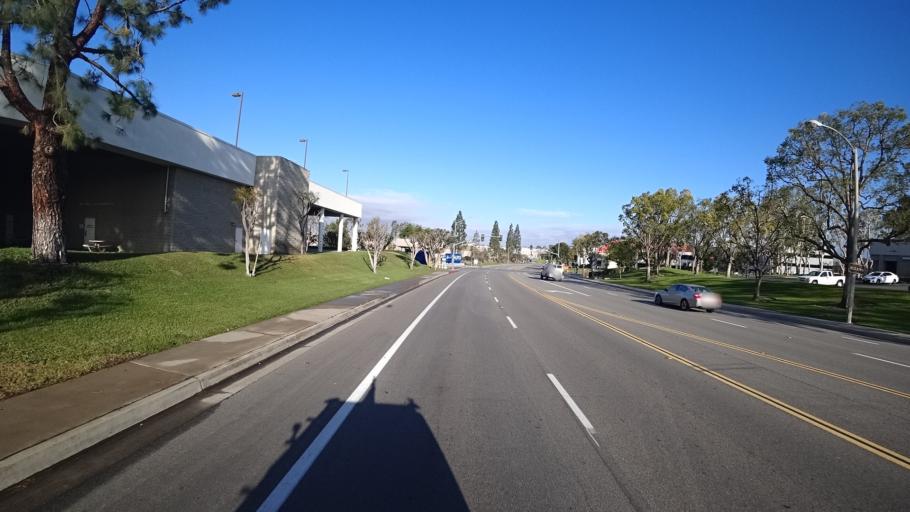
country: US
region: California
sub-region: Orange County
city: Laguna Hills
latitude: 33.6326
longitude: -117.7200
